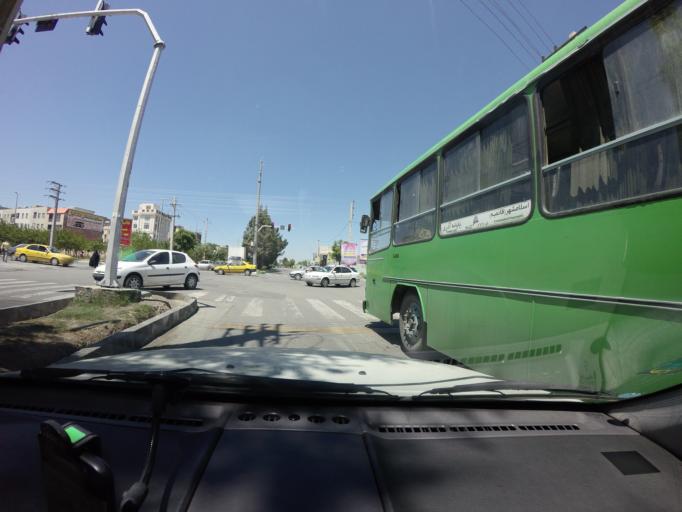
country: IR
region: Tehran
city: Eslamshahr
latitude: 35.5337
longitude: 51.2174
